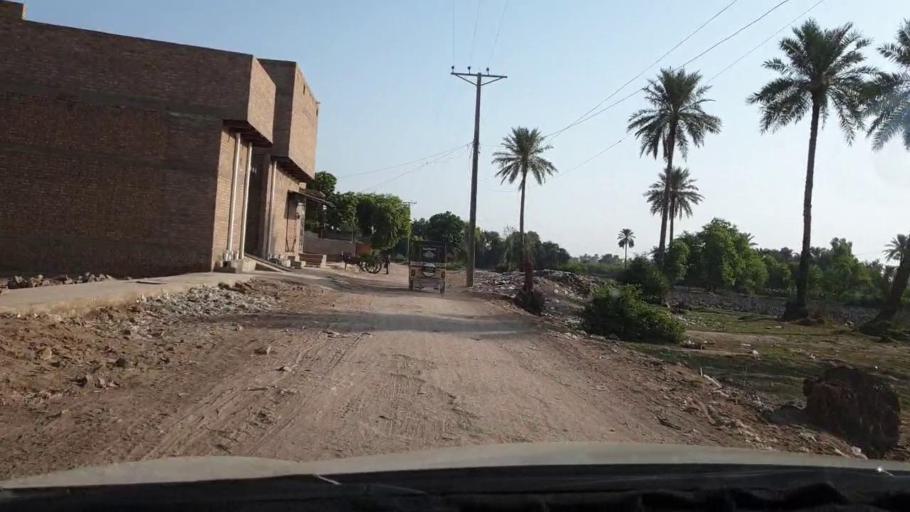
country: PK
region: Sindh
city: Larkana
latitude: 27.5489
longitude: 68.2312
